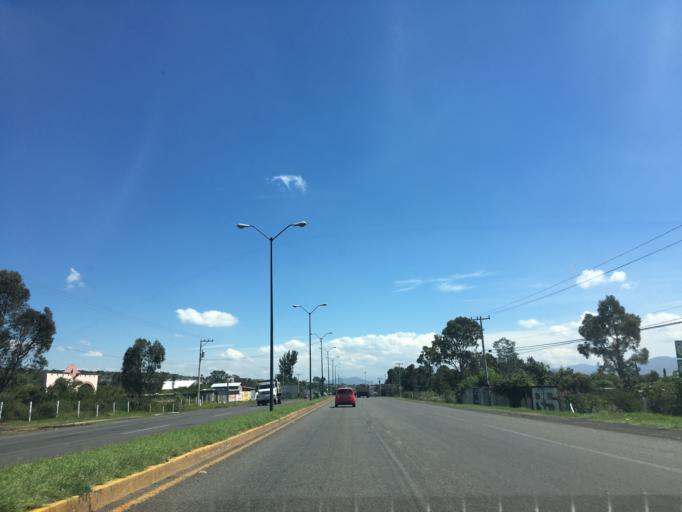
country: MX
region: Michoacan
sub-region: Morelia
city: Conjunto Habitacional Villas del Pedregal
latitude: 19.6871
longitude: -101.3129
